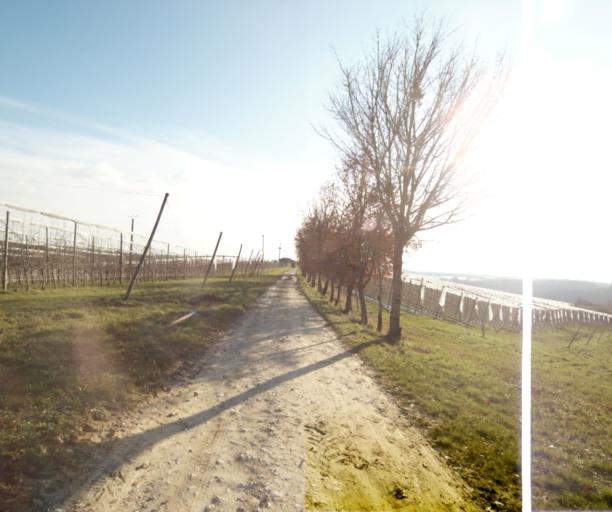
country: FR
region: Midi-Pyrenees
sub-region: Departement du Tarn-et-Garonne
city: Moissac
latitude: 44.1364
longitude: 1.0482
